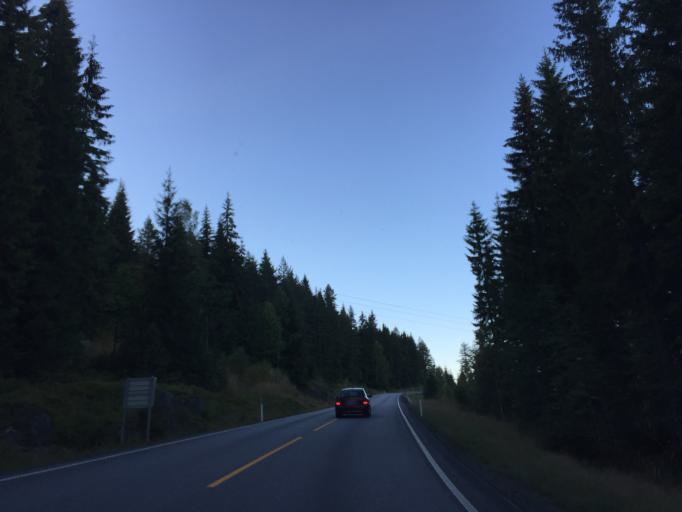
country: NO
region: Hedmark
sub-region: Nord-Odal
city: Sand
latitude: 60.4619
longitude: 11.5099
